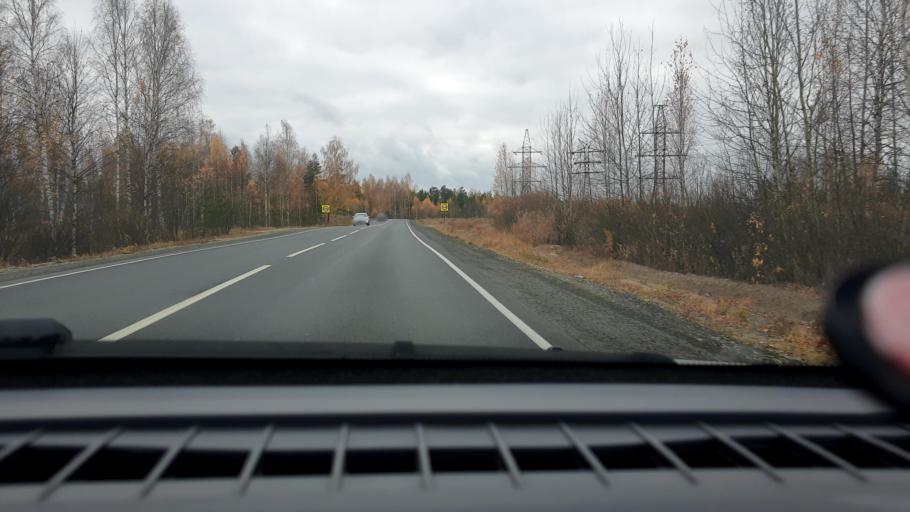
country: RU
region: Nizjnij Novgorod
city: Lukino
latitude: 56.3688
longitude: 43.6175
